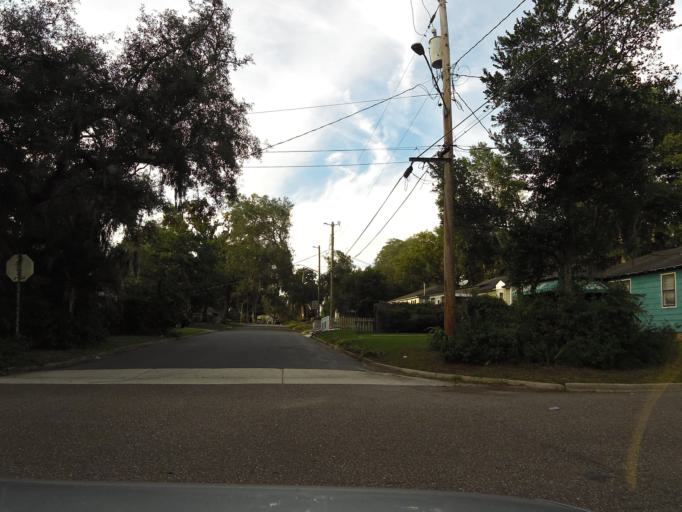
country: US
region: Florida
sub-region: Duval County
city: Jacksonville
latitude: 30.3850
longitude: -81.6615
